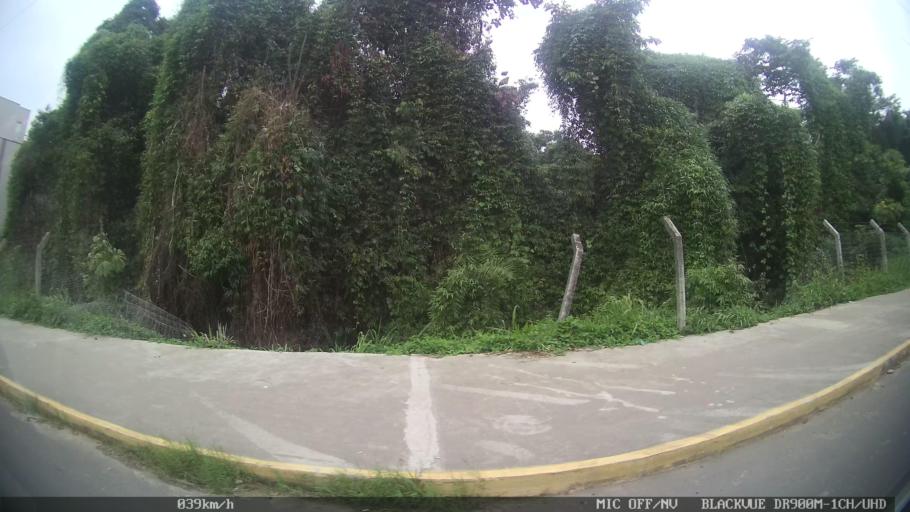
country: BR
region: Santa Catarina
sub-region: Joinville
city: Joinville
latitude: -26.2836
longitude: -48.8151
